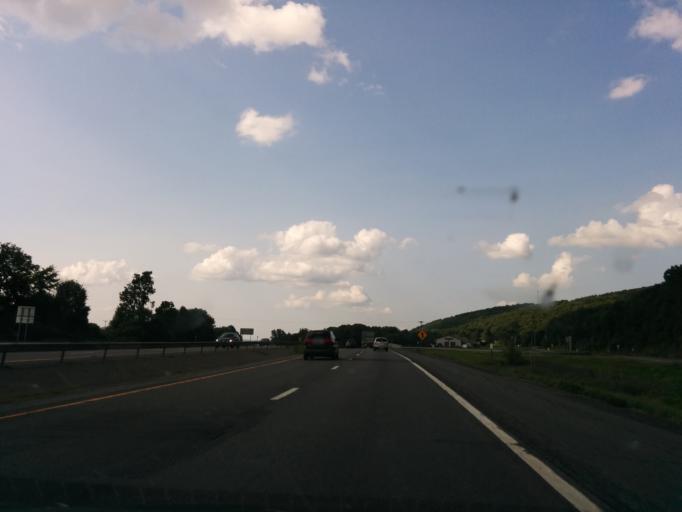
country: US
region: New York
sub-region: Onondaga County
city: Nedrow
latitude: 42.8070
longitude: -76.1215
